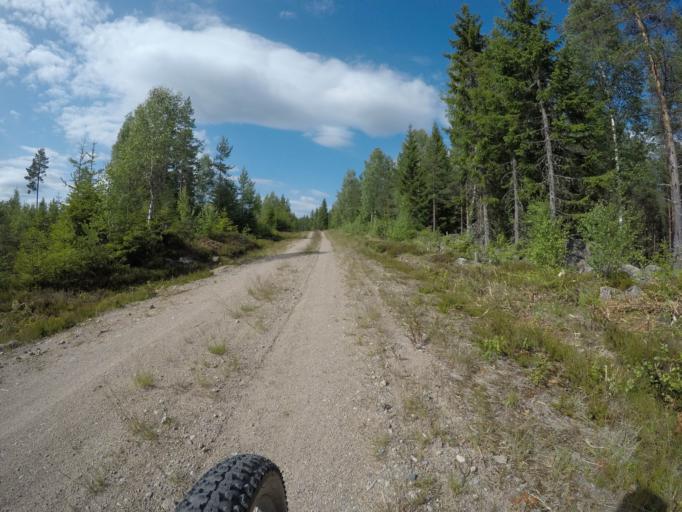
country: SE
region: Dalarna
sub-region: Ludvika Kommun
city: Abborrberget
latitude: 60.0534
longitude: 14.5762
